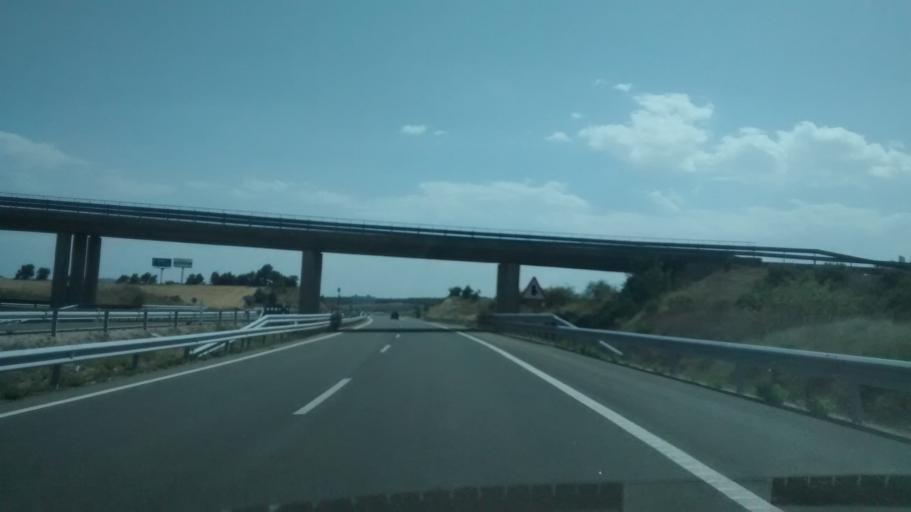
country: ES
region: Basque Country
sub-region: Provincia de Alava
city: Arminon
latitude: 42.7083
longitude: -2.9030
